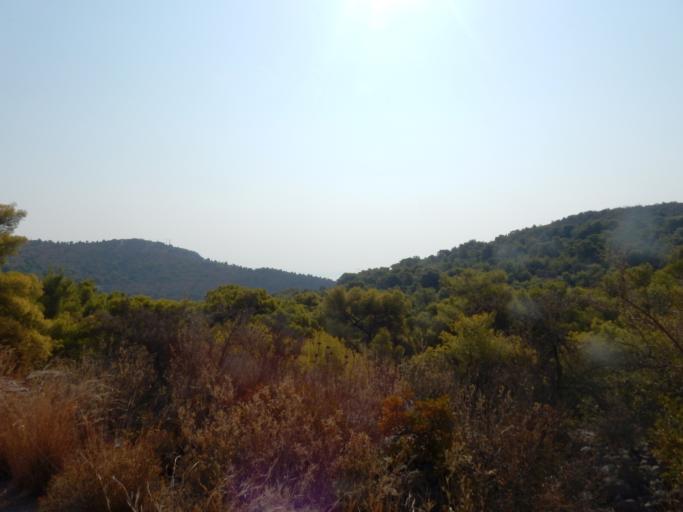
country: GR
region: Attica
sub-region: Nomos Piraios
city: Vathi
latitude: 37.7216
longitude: 23.5214
